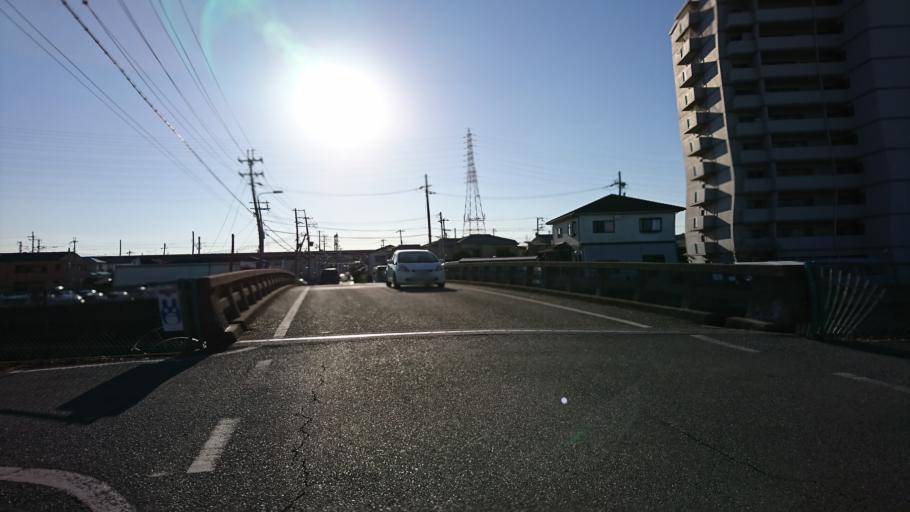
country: JP
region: Hyogo
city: Kakogawacho-honmachi
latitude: 34.7431
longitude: 134.8360
